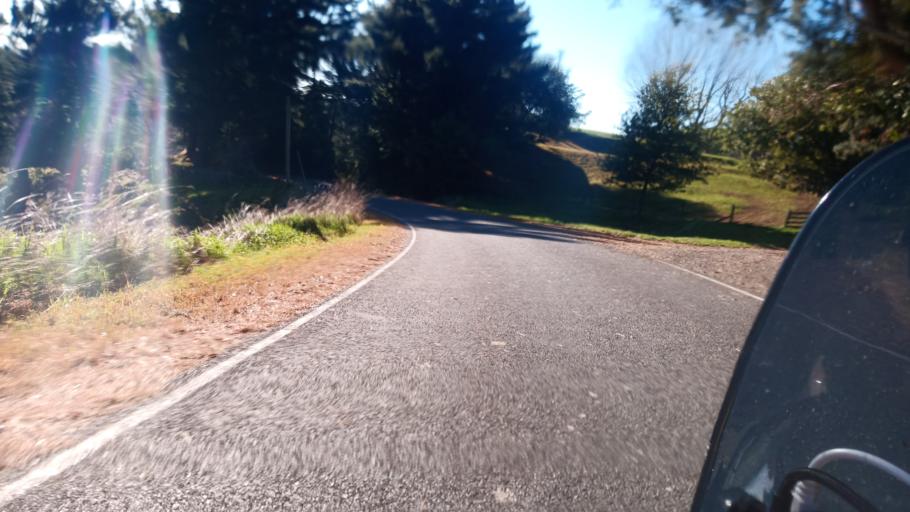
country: NZ
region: Hawke's Bay
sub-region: Wairoa District
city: Wairoa
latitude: -38.8295
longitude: 177.2891
